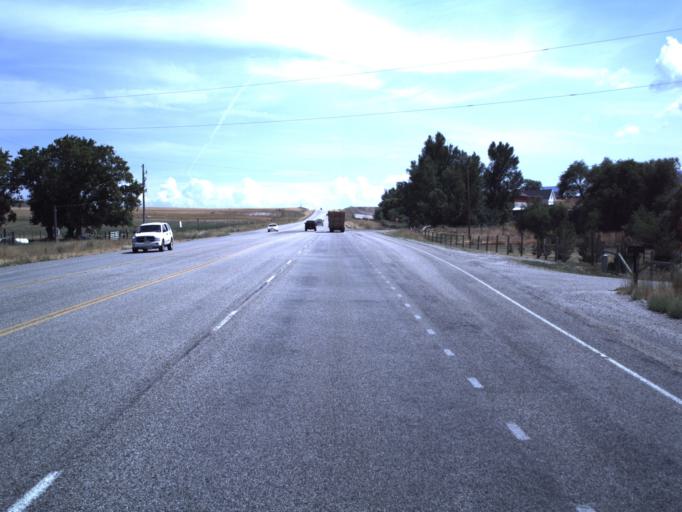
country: US
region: Utah
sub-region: Cache County
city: Mendon
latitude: 41.7875
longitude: -112.0286
